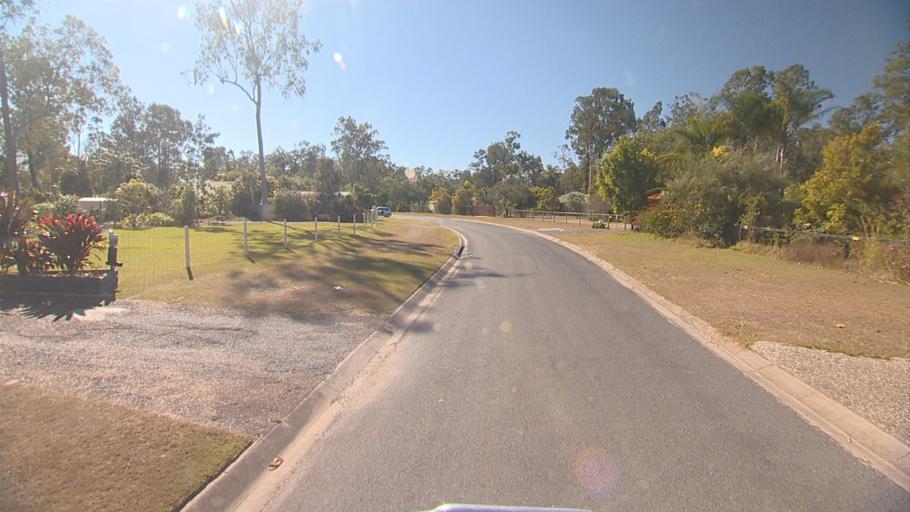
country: AU
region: Queensland
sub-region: Logan
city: North Maclean
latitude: -27.8166
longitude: 152.9503
